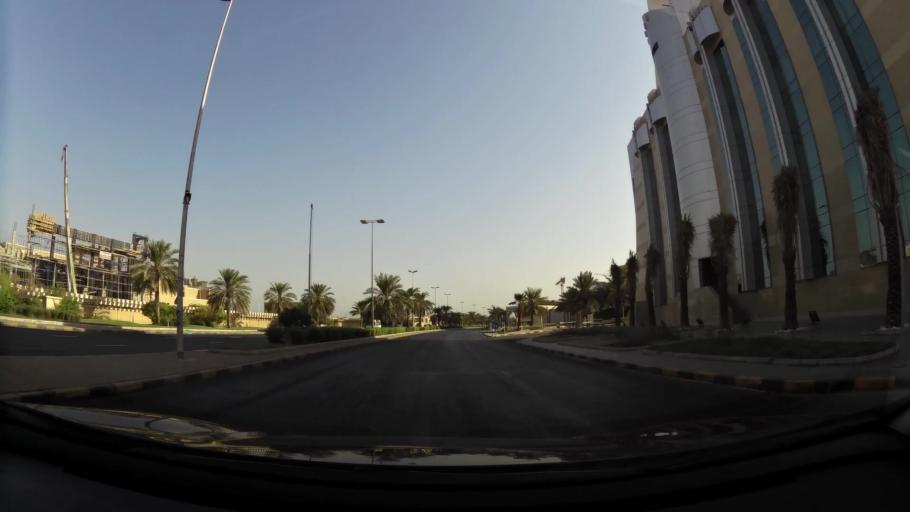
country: KW
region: Al Asimah
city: Kuwait City
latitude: 29.3815
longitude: 47.9748
